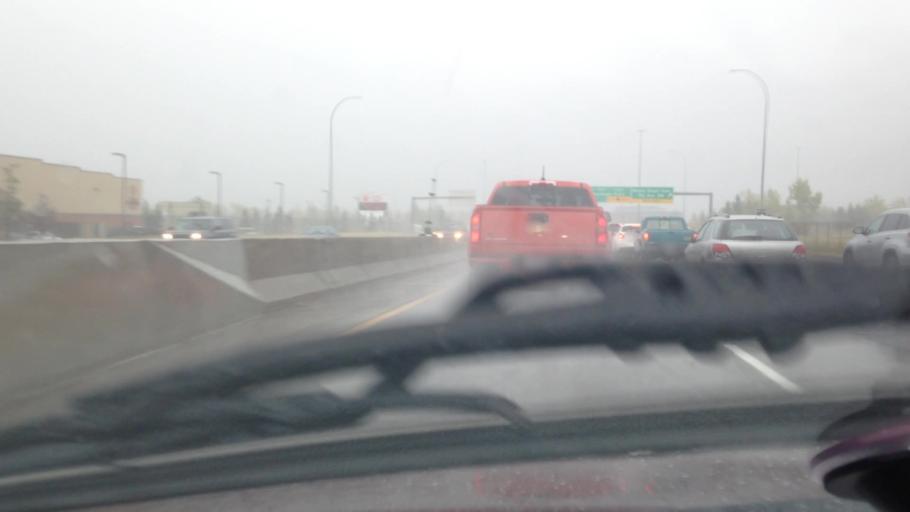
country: CA
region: Alberta
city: Calgary
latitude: 51.0129
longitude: -114.1181
